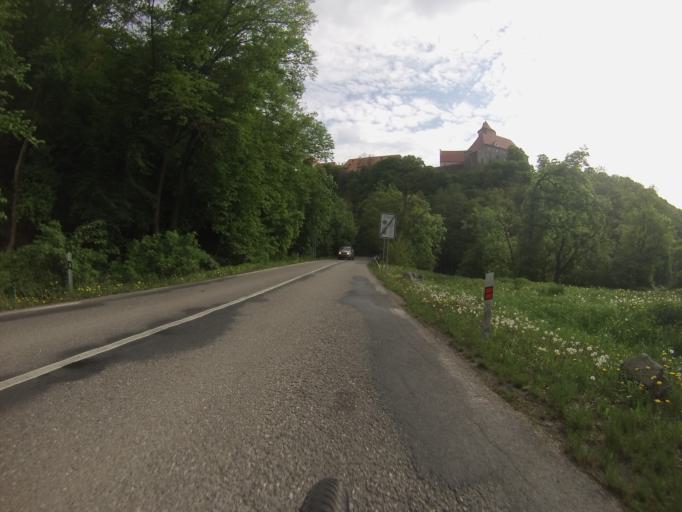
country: CZ
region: South Moravian
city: Veverska Bityska
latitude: 49.2579
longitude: 16.4640
